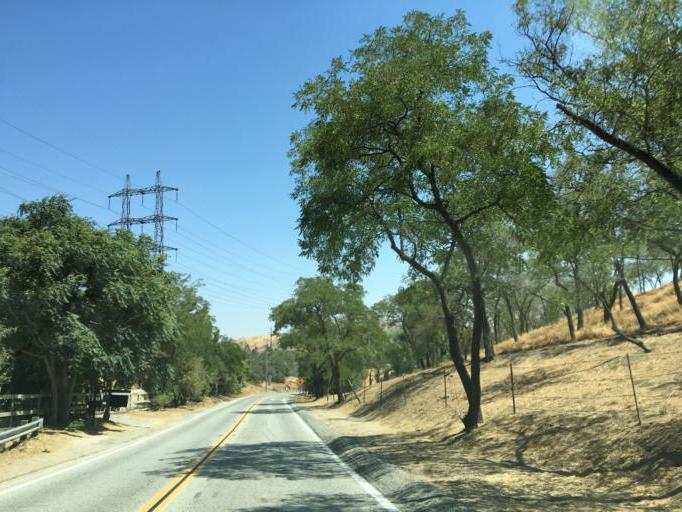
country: US
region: California
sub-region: Los Angeles County
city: Green Valley
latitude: 34.6471
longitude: -118.3773
